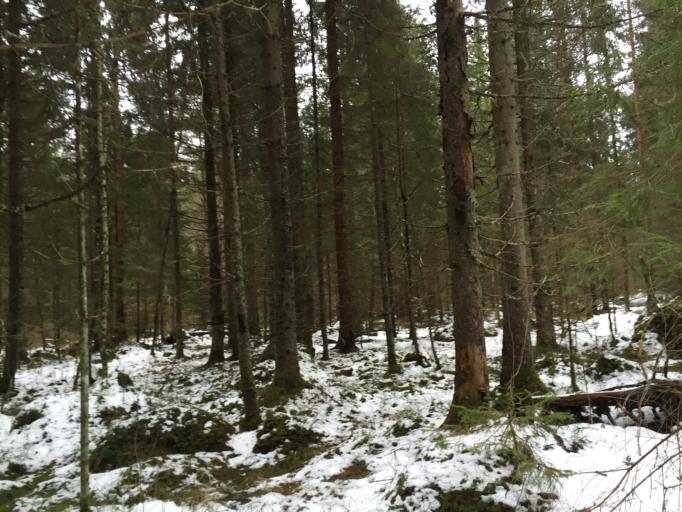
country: LV
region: Garkalne
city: Garkalne
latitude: 56.9660
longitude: 24.4731
